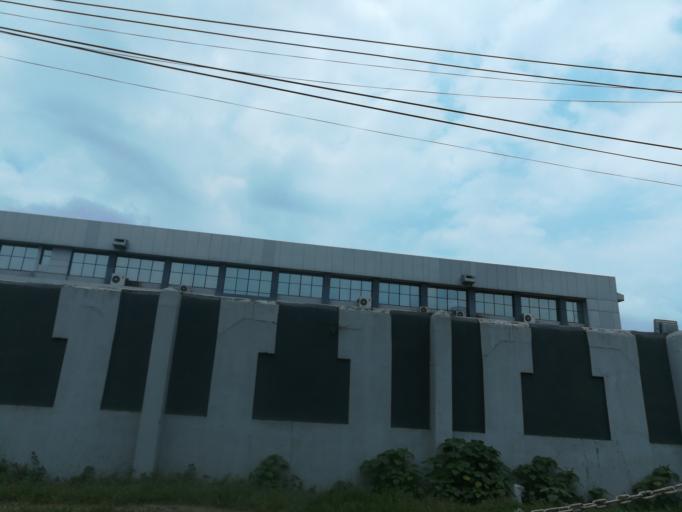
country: NG
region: Lagos
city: Lagos
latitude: 6.4502
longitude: 3.4008
